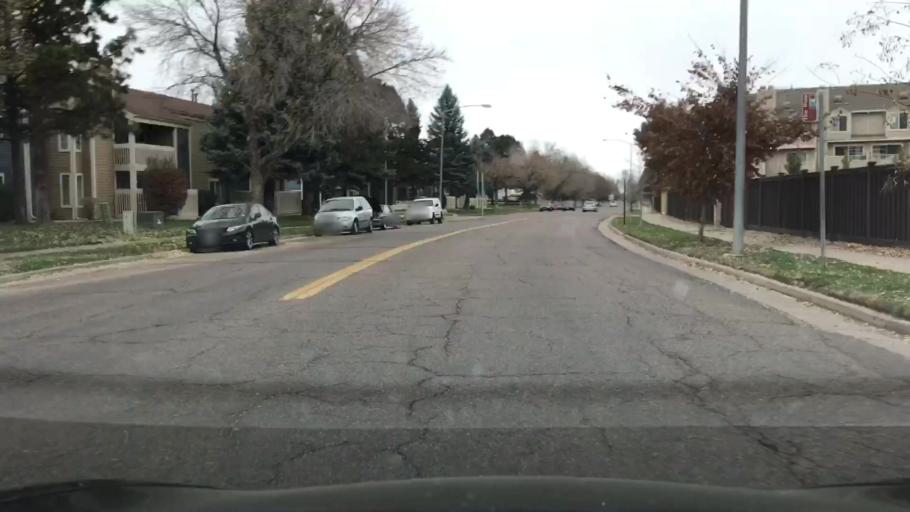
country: US
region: Colorado
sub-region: Arapahoe County
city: Glendale
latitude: 39.6837
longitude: -104.8907
